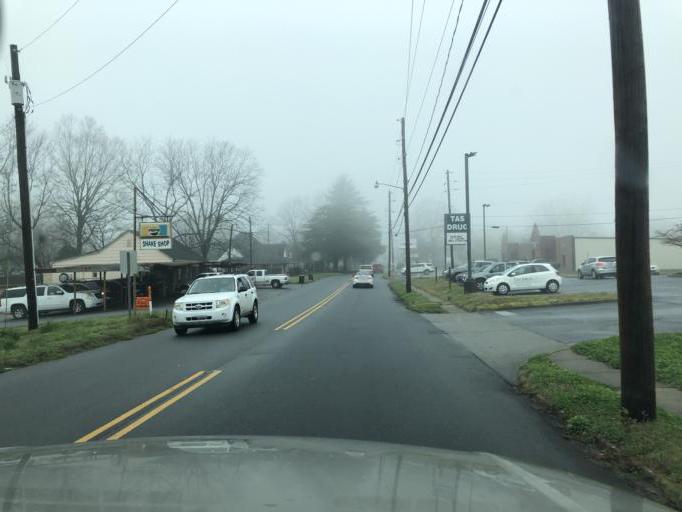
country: US
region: North Carolina
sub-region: Gaston County
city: Cherryville
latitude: 35.3804
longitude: -81.3856
